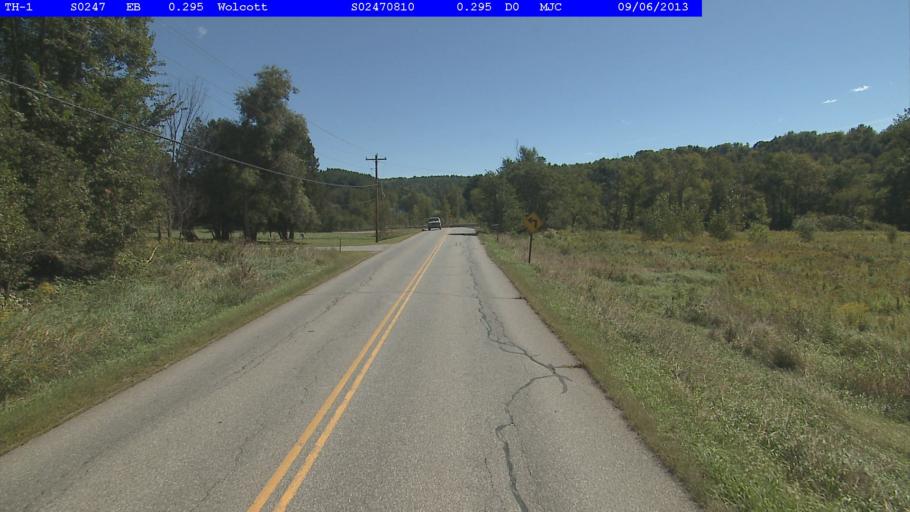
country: US
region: Vermont
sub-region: Lamoille County
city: Morrisville
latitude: 44.5640
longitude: -72.4891
